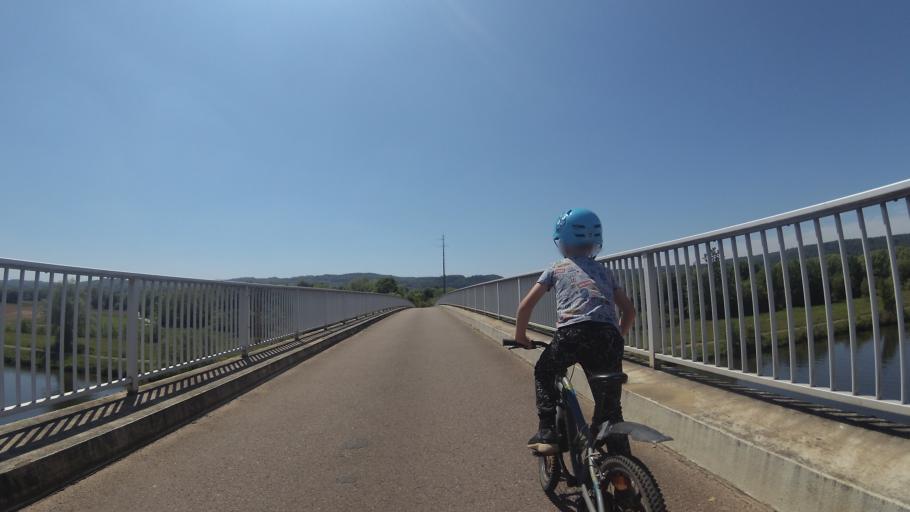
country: DE
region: Saarland
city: Mettlach
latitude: 49.4685
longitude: 6.6072
